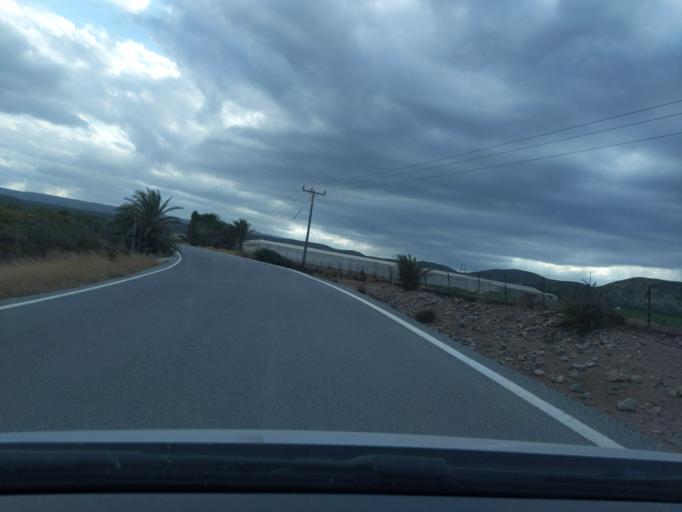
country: GR
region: Crete
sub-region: Nomos Lasithiou
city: Palekastro
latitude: 35.2617
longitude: 26.2574
